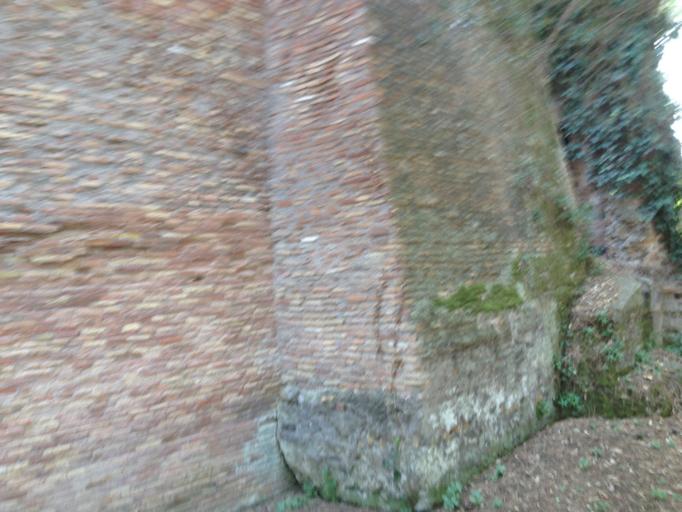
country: IT
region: Latium
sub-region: Citta metropolitana di Roma Capitale
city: Rome
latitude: 41.8579
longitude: 12.5242
